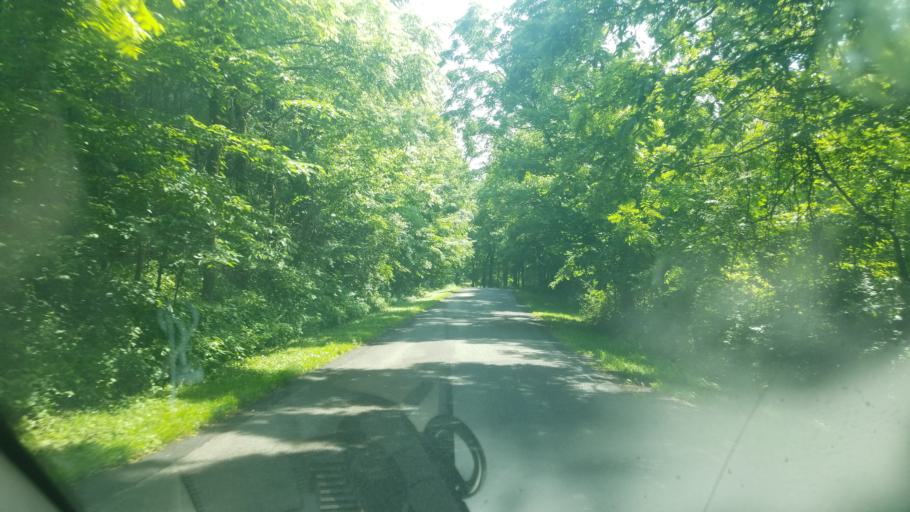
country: US
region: Ohio
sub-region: Champaign County
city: North Lewisburg
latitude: 40.2804
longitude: -83.6404
